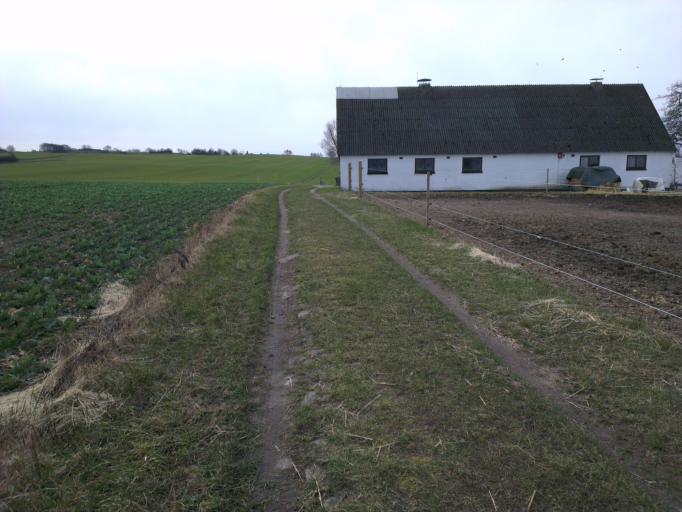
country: DK
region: Capital Region
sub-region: Frederikssund Kommune
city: Skibby
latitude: 55.7883
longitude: 11.8682
